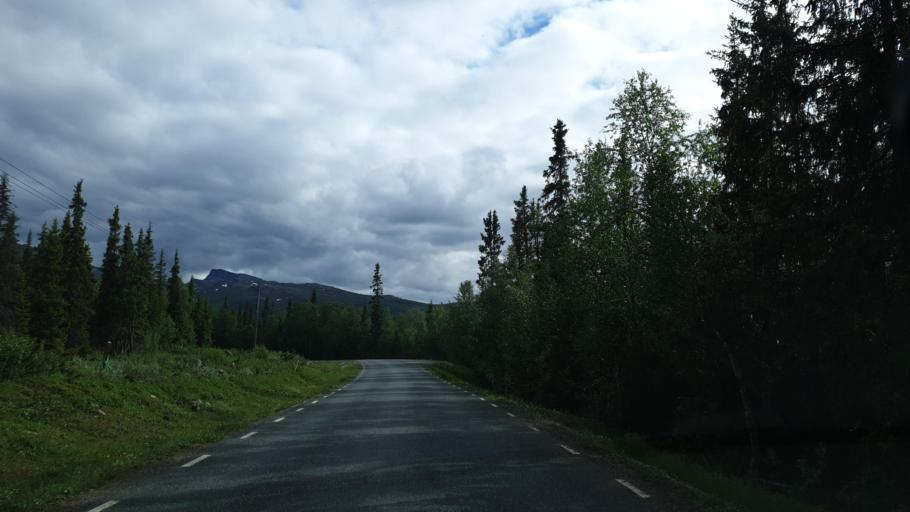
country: SE
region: Vaesterbotten
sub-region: Vilhelmina Kommun
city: Sjoberg
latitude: 65.2712
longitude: 15.3682
